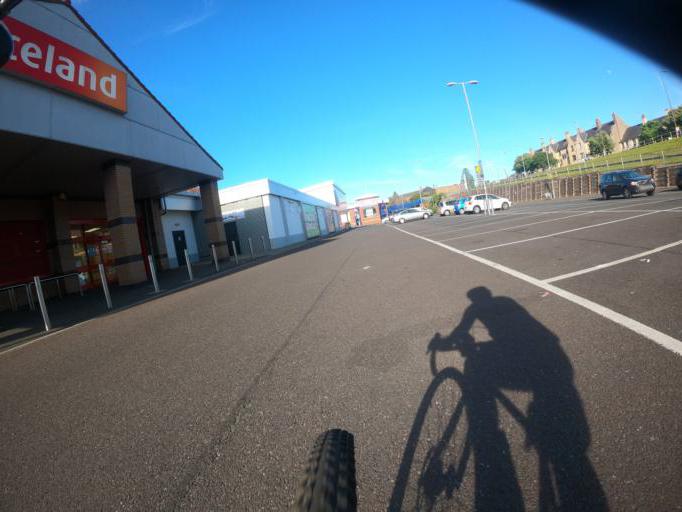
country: GB
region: Scotland
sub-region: Edinburgh
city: Edinburgh
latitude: 55.9787
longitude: -3.2345
